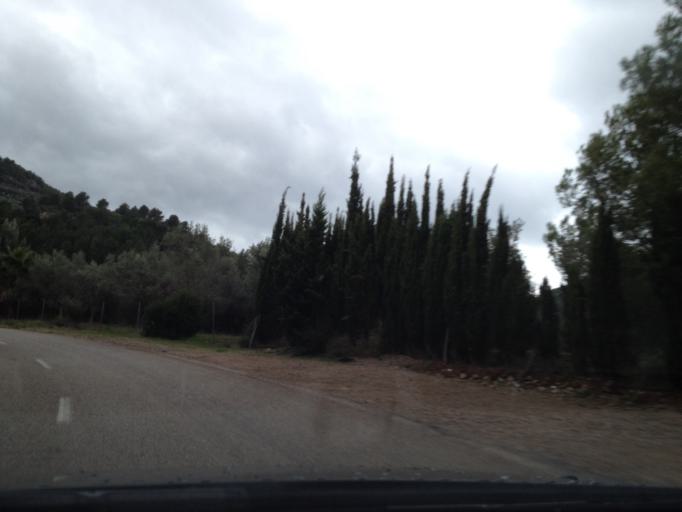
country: ES
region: Balearic Islands
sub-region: Illes Balears
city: Soller
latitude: 39.7757
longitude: 2.6910
